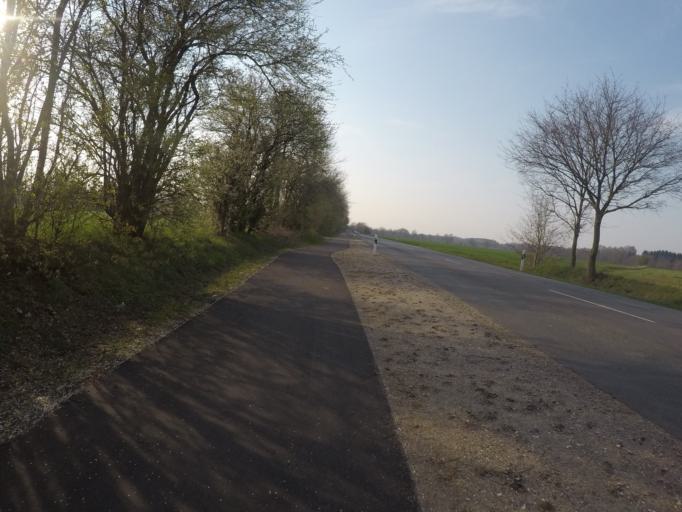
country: DE
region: Schleswig-Holstein
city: Rickling
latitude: 53.9897
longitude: 10.1800
